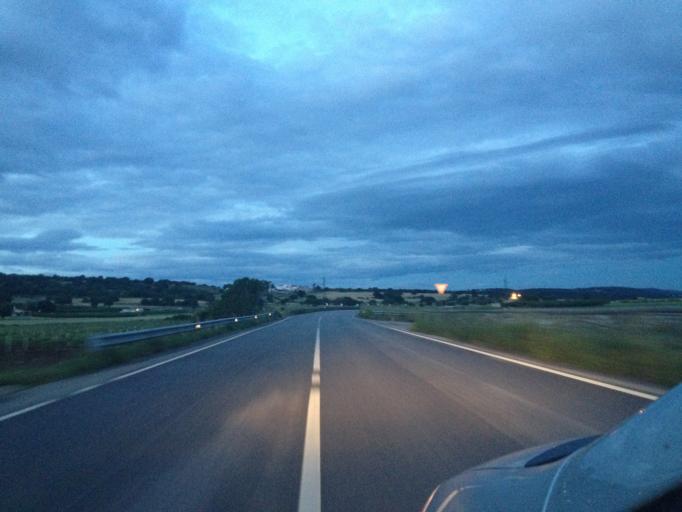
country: IT
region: Apulia
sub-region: Provincia di Bari
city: Alberobello
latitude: 40.8255
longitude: 17.2340
